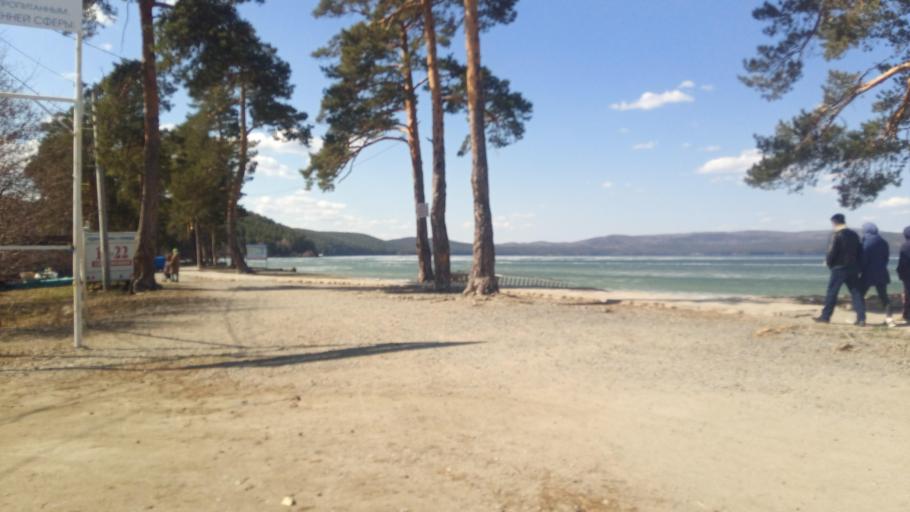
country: RU
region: Chelyabinsk
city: Turgoyak
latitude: 55.1526
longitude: 60.1099
